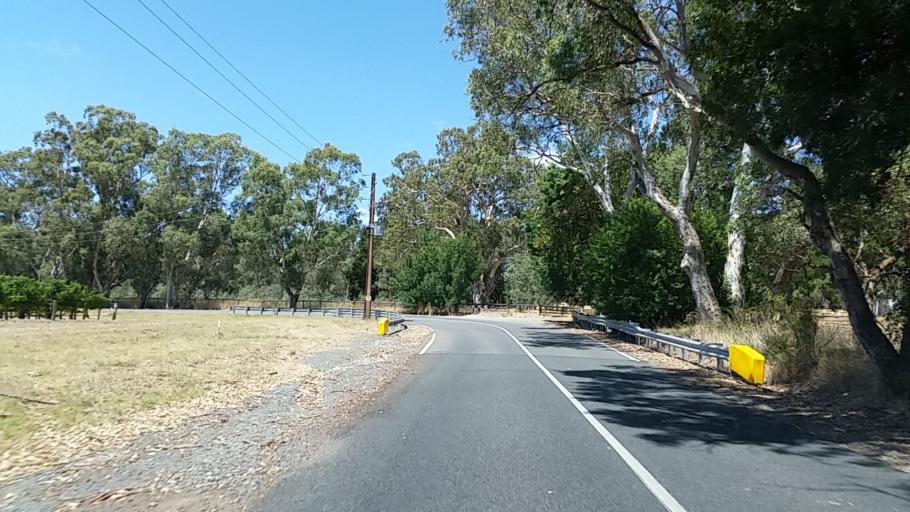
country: AU
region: South Australia
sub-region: Adelaide Hills
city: Woodside
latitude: -34.9678
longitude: 138.8788
